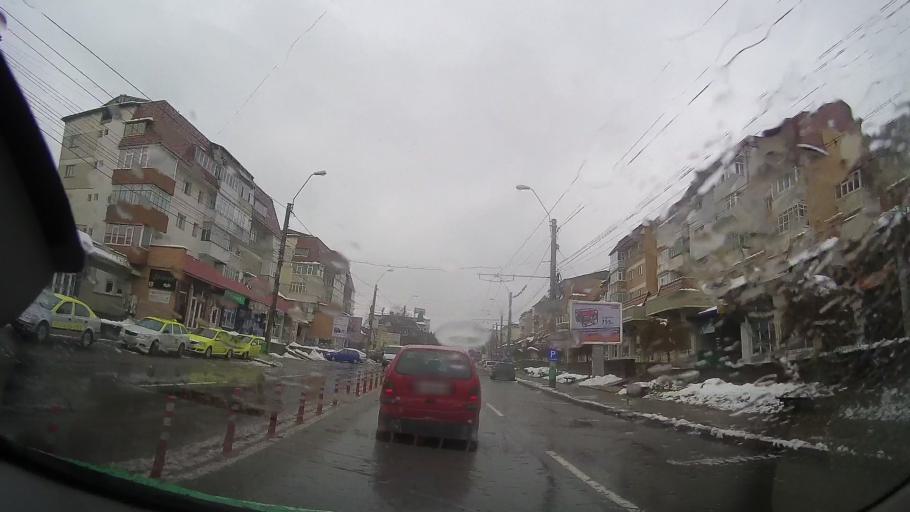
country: RO
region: Neamt
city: Piatra Neamt
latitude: 46.9357
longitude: 26.3523
